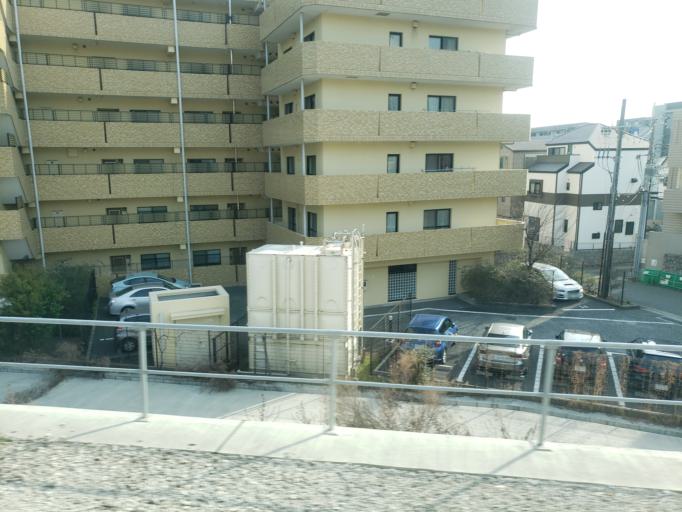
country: JP
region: Hyogo
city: Nishinomiya-hama
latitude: 34.7389
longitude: 135.3276
